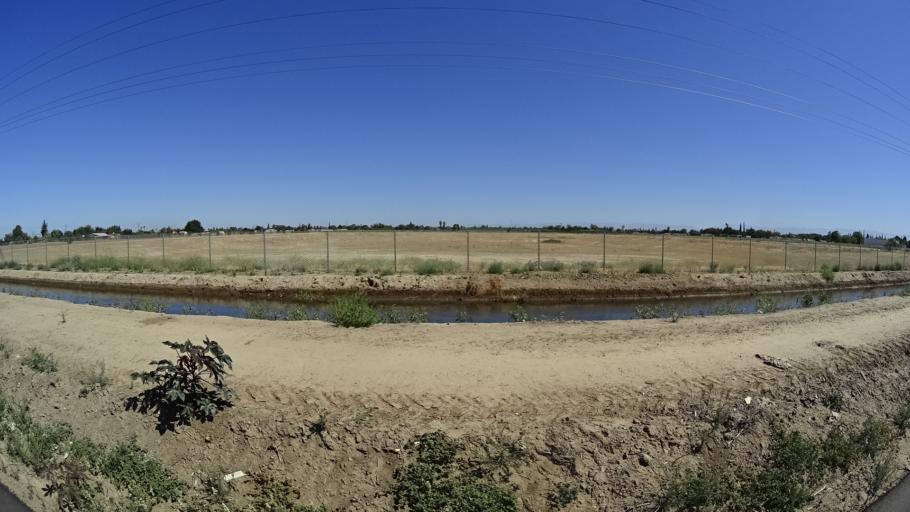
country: US
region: California
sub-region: Fresno County
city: West Park
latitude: 36.6994
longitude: -119.8058
